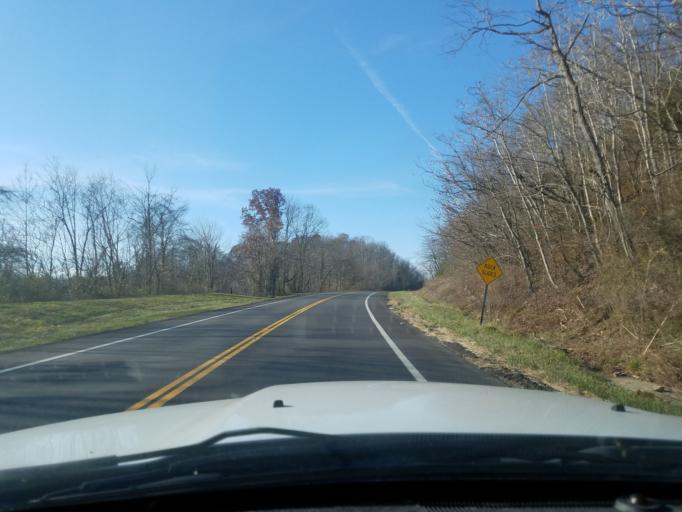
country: US
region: Ohio
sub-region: Washington County
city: Marietta
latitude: 39.4046
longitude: -81.4769
